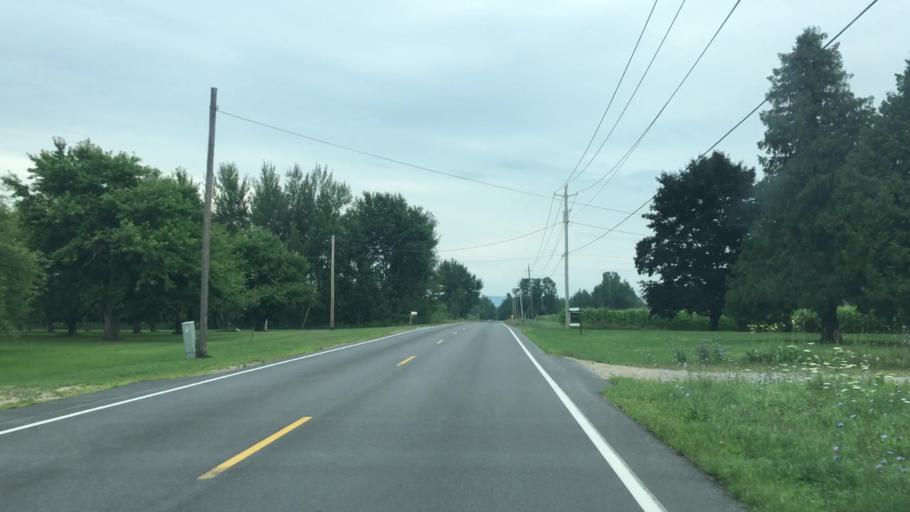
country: US
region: New York
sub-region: Clinton County
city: Peru
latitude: 44.5893
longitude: -73.5718
